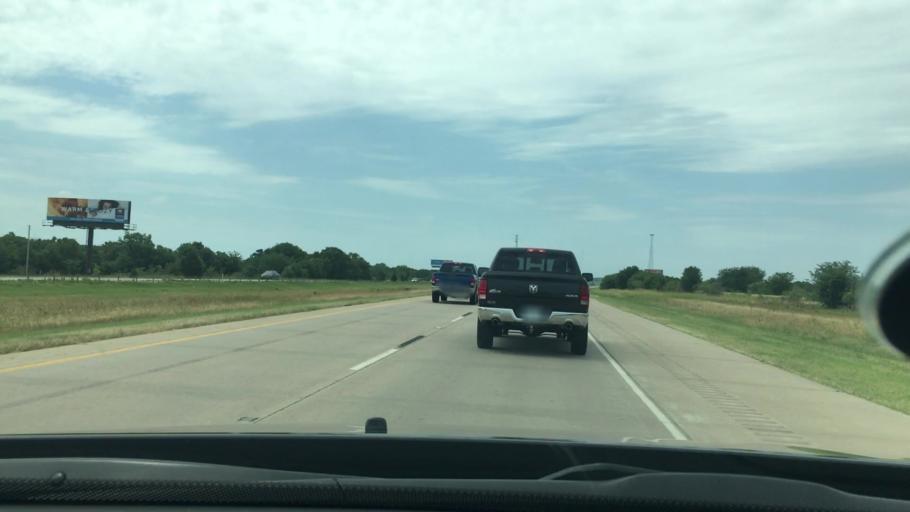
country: US
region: Oklahoma
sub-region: Carter County
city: Ardmore
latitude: 34.2862
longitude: -97.1599
